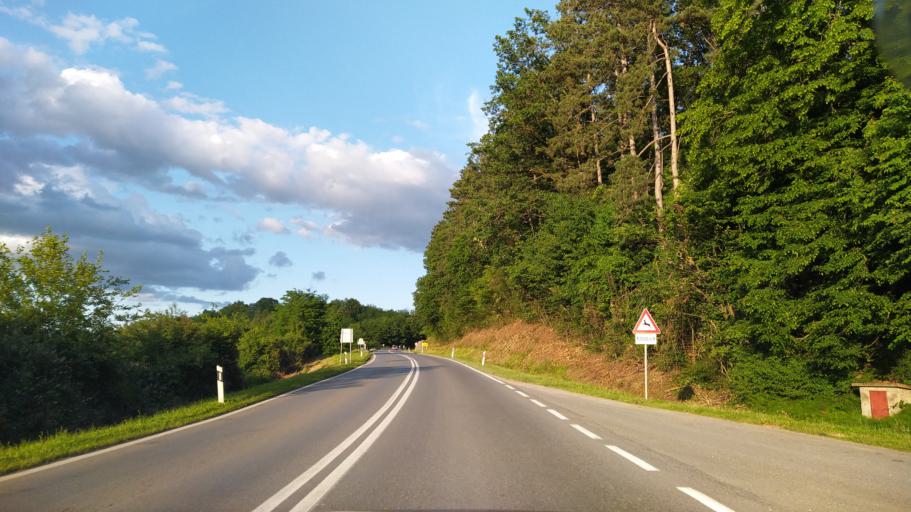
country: HR
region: Osjecko-Baranjska
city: Martin
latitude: 45.4905
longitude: 18.0299
